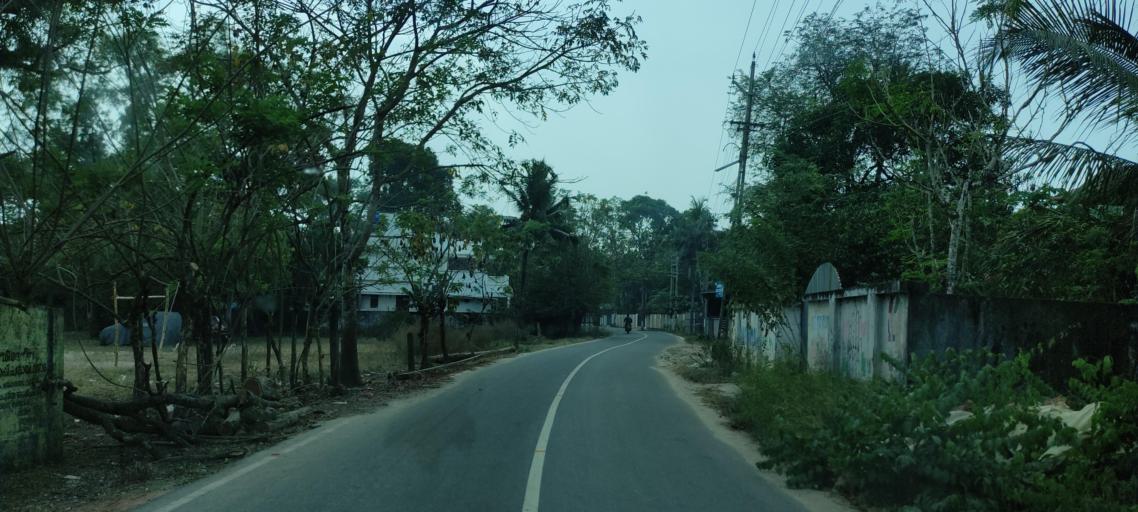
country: IN
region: Kerala
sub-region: Alappuzha
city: Alleppey
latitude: 9.5732
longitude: 76.3391
